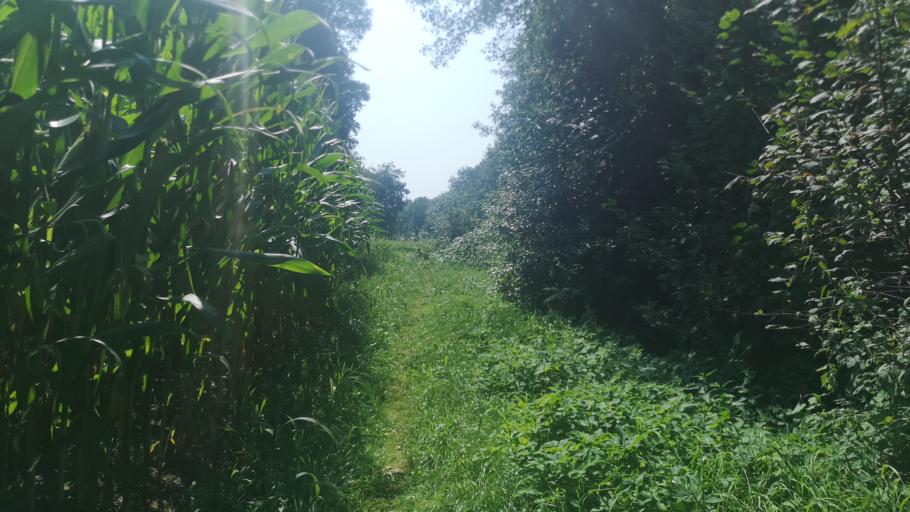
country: AT
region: Styria
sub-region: Politischer Bezirk Deutschlandsberg
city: Lannach
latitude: 46.9386
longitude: 15.3380
